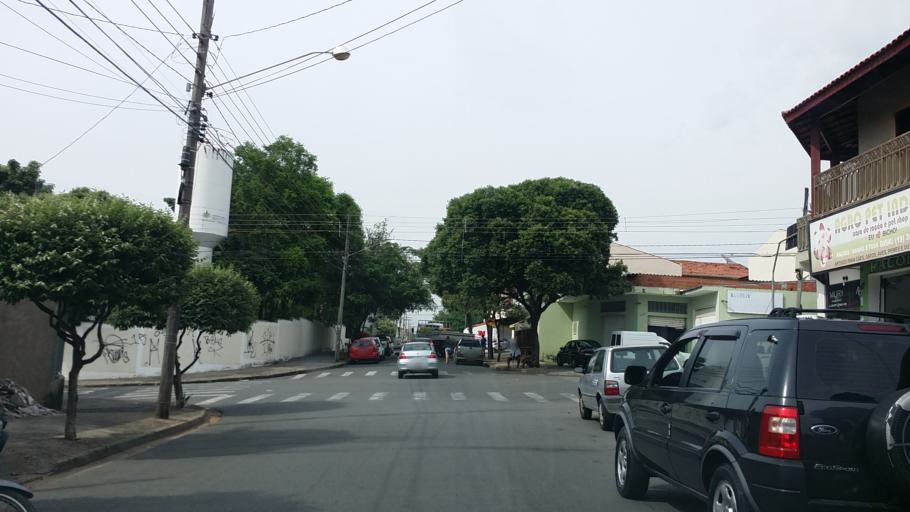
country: BR
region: Sao Paulo
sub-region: Indaiatuba
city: Indaiatuba
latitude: -23.1219
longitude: -47.2371
